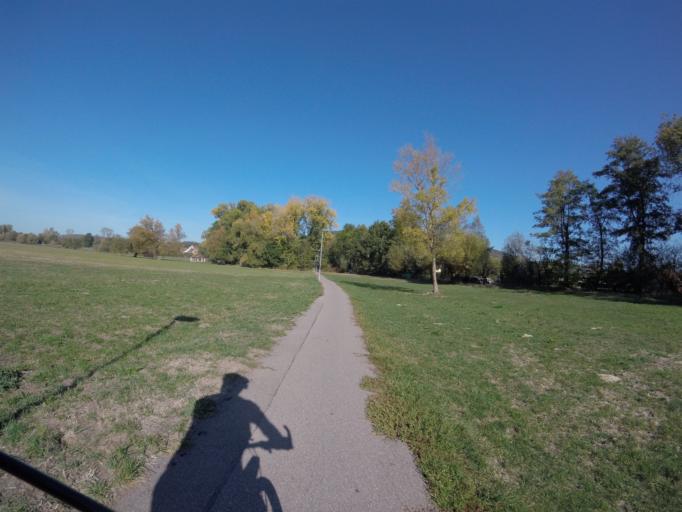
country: DE
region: Baden-Wuerttemberg
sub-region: Regierungsbezirk Stuttgart
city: Sersheim
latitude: 48.9816
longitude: 8.9861
